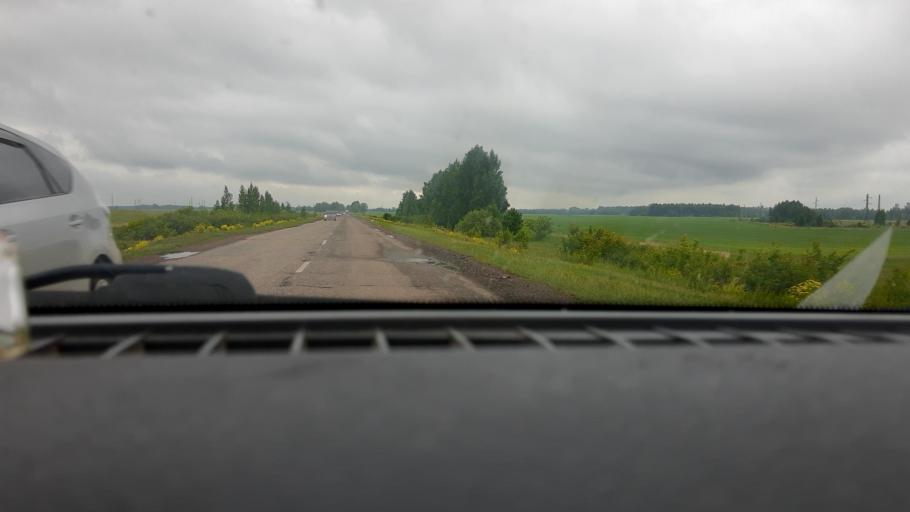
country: RU
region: Bashkortostan
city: Priyutovo
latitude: 53.9246
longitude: 53.9627
